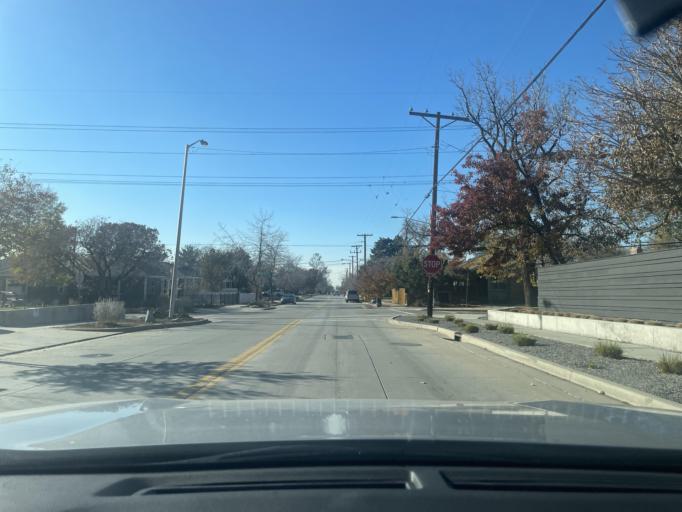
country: US
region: Utah
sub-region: Salt Lake County
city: Willard
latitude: 40.7417
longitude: -111.8360
